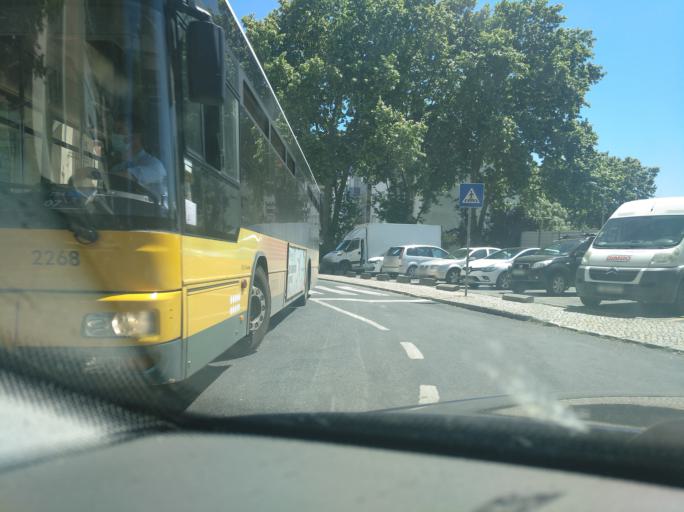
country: PT
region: Lisbon
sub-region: Amadora
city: Amadora
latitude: 38.7411
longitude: -9.2117
